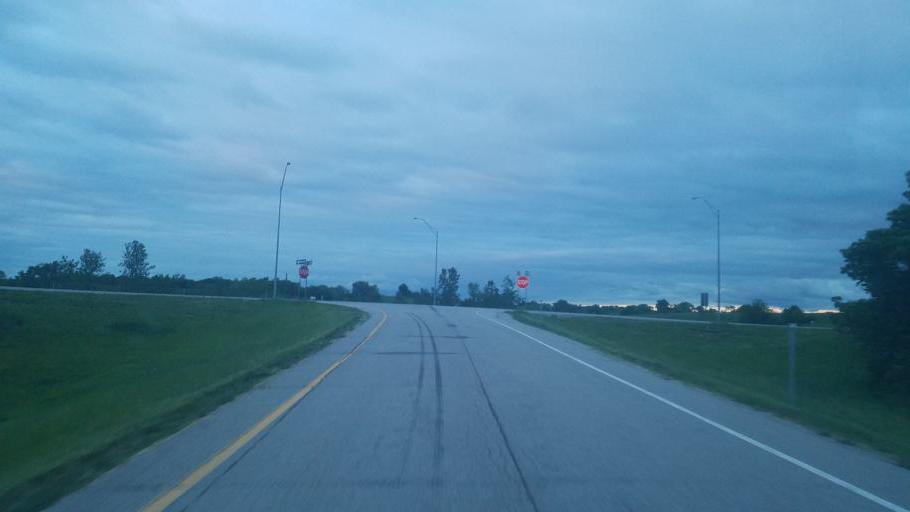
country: US
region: Iowa
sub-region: Decatur County
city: Lamoni
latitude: 40.6229
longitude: -93.8882
